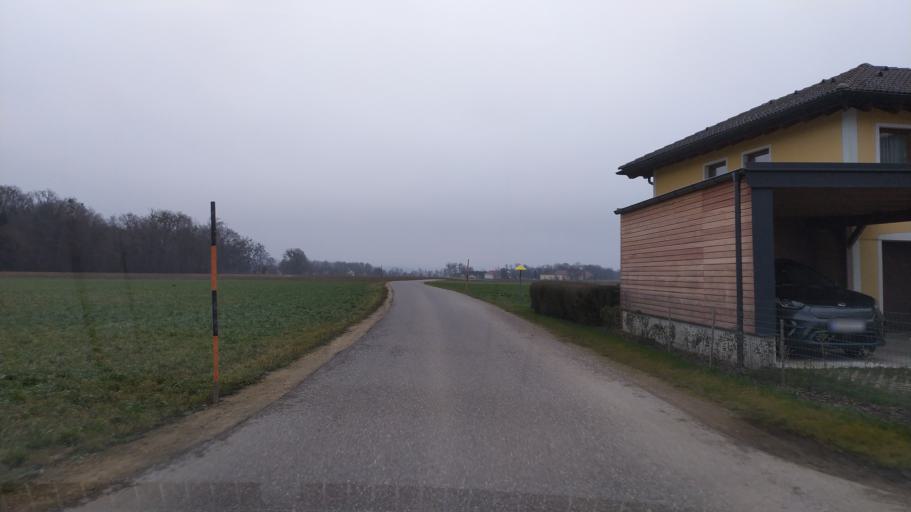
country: AT
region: Upper Austria
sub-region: Politischer Bezirk Perg
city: Perg
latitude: 48.2059
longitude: 14.7224
